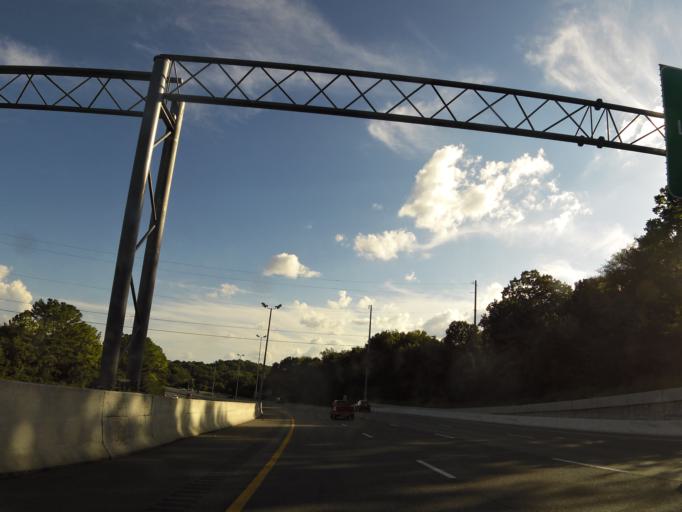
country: US
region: Tennessee
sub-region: Davidson County
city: Lakewood
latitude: 36.1828
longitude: -86.6944
